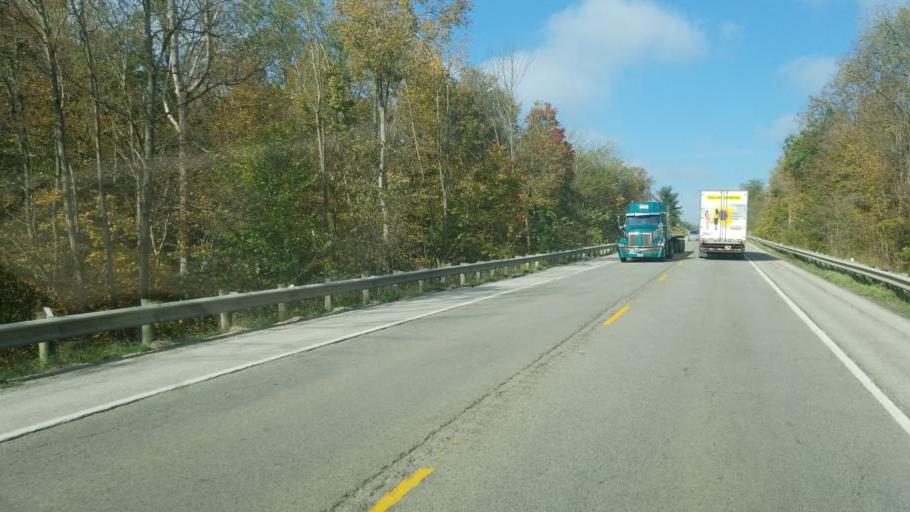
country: US
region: Ohio
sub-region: Stark County
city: Brewster
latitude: 40.6726
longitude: -81.6578
